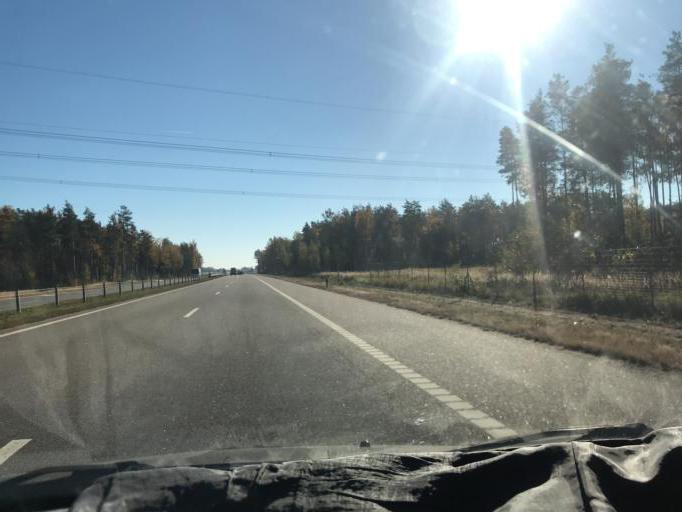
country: BY
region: Mogilev
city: Yalizava
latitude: 53.2592
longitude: 28.9016
